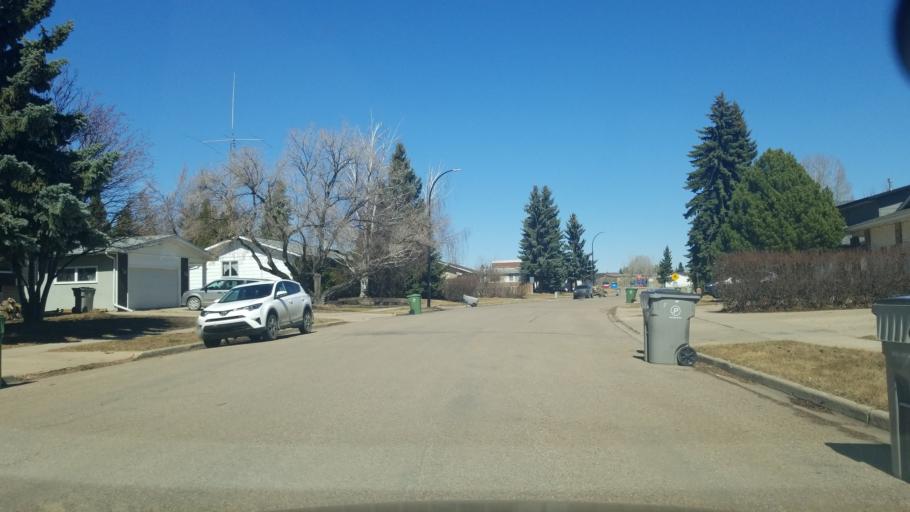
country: CA
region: Saskatchewan
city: Lloydminster
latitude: 53.2646
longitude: -110.0124
